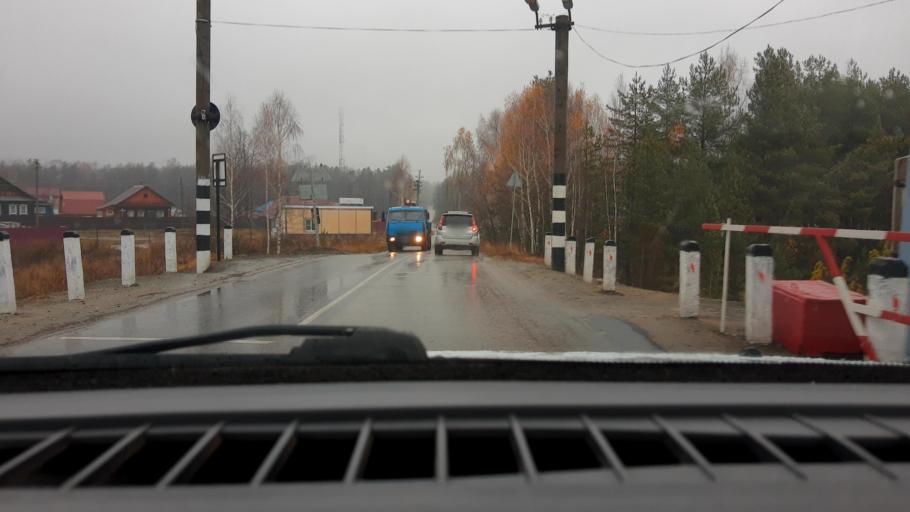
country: RU
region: Nizjnij Novgorod
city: Linda
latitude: 56.6853
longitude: 44.2021
